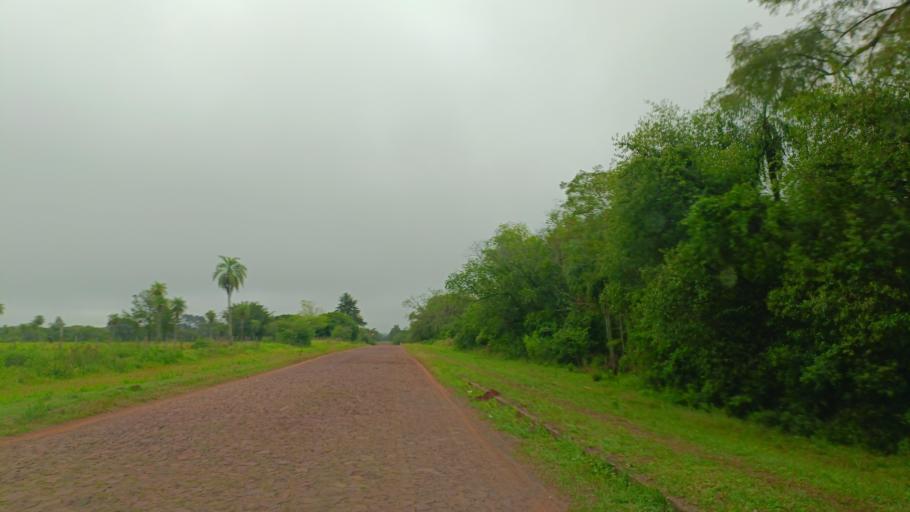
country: PY
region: Misiones
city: Santa Maria
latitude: -26.8757
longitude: -57.0124
